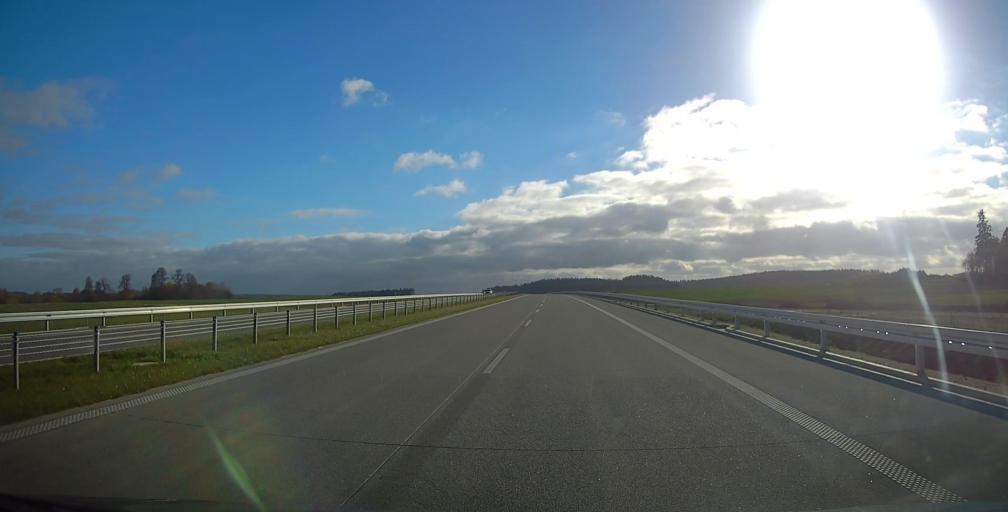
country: PL
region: Warmian-Masurian Voivodeship
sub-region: Powiat elcki
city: Elk
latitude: 53.7144
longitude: 22.2807
